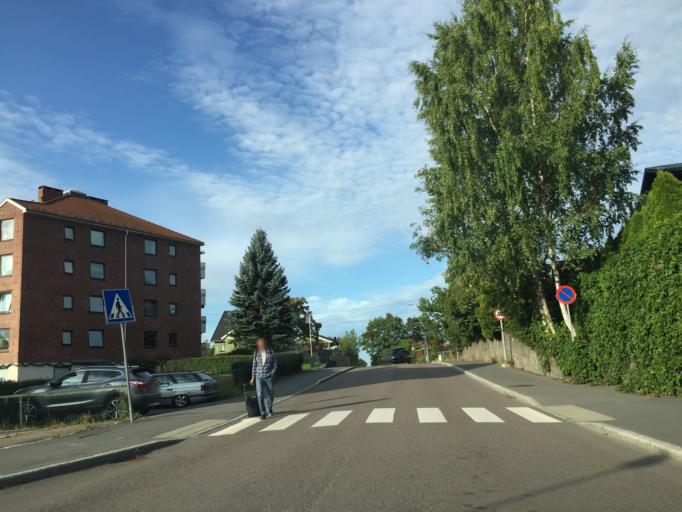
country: NO
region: Akershus
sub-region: Oppegard
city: Kolbotn
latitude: 59.8733
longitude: 10.8097
